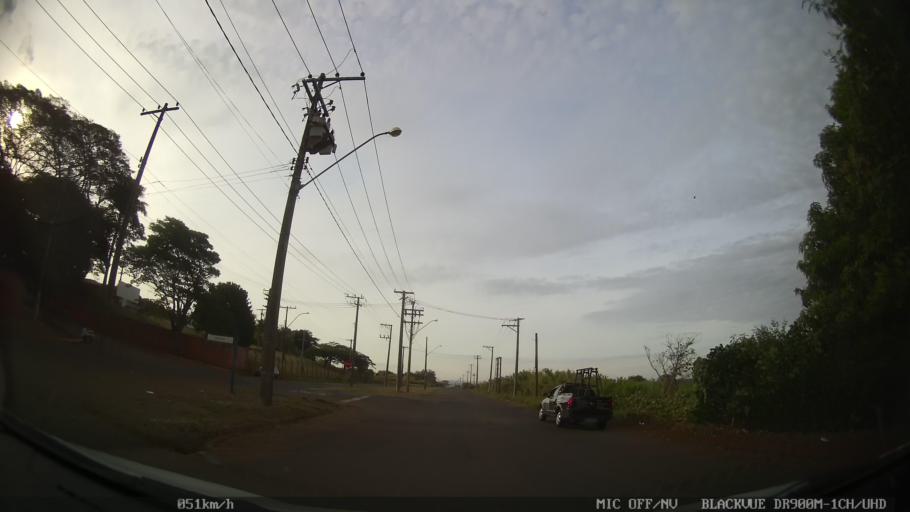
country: BR
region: Sao Paulo
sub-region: Piracicaba
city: Piracicaba
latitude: -22.7270
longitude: -47.5858
